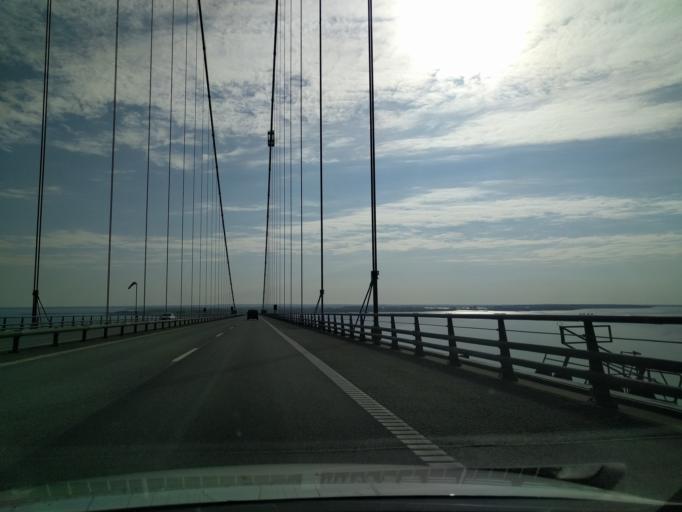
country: DK
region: Zealand
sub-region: Slagelse Kommune
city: Korsor
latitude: 55.3439
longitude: 11.0485
